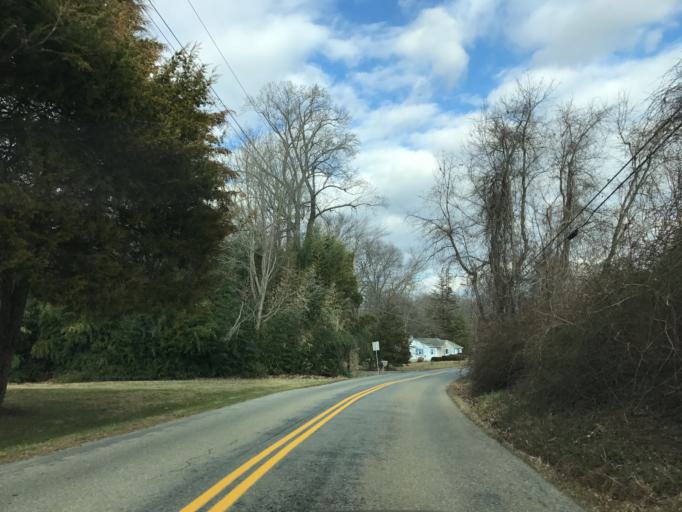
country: US
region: Maryland
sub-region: Harford County
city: Havre de Grace
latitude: 39.6442
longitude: -76.1852
